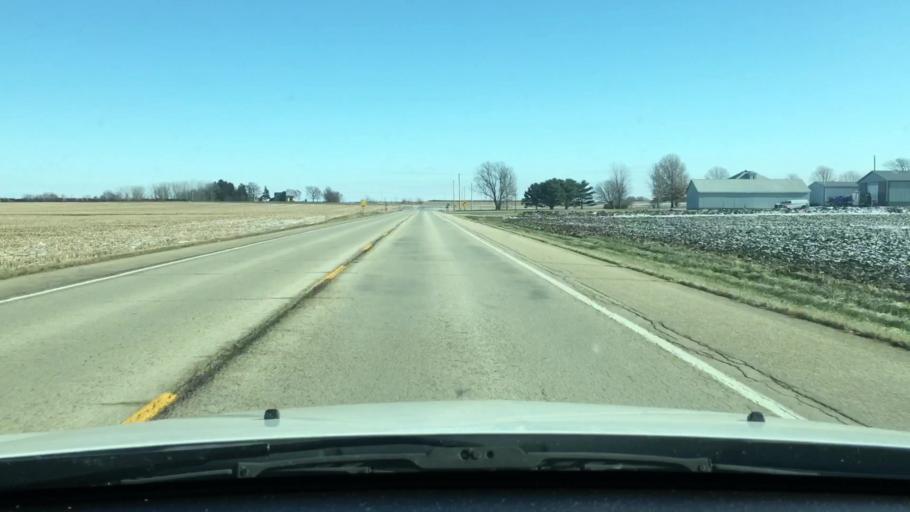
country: US
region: Illinois
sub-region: DeKalb County
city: Malta
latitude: 42.0079
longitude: -88.9467
